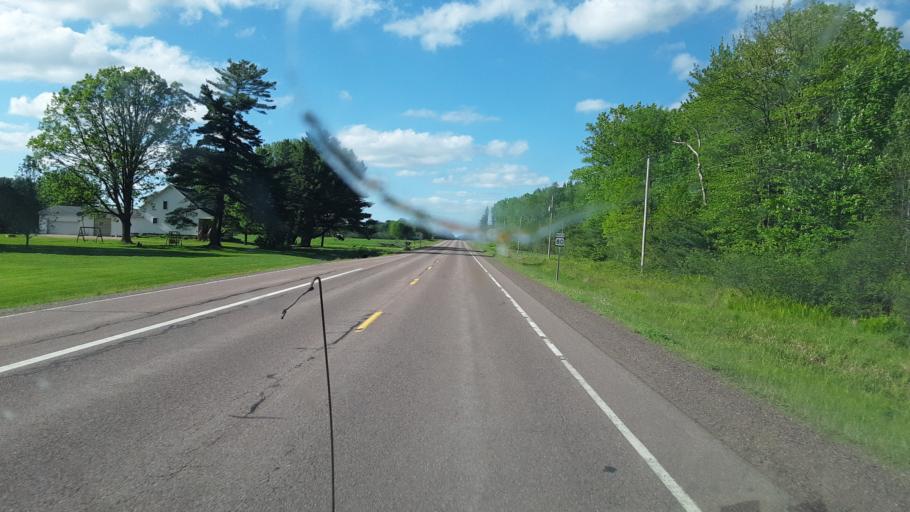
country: US
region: Wisconsin
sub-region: Wood County
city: Marshfield
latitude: 44.4972
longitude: -90.1802
